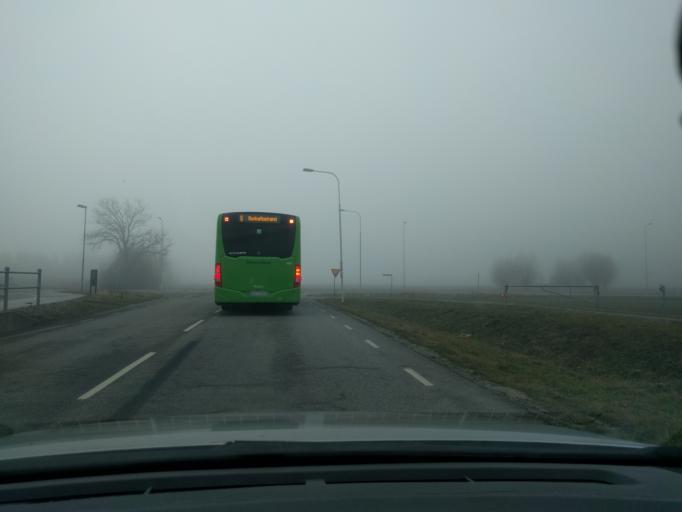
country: SE
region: Skane
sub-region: Malmo
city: Bunkeflostrand
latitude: 55.5587
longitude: 12.9679
